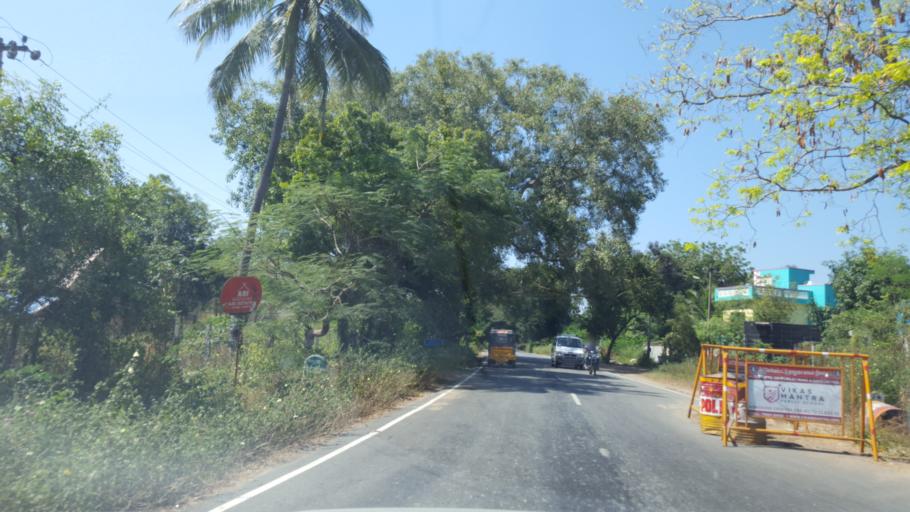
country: IN
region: Tamil Nadu
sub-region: Kancheepuram
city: Chengalpattu
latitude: 12.7356
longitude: 79.9441
